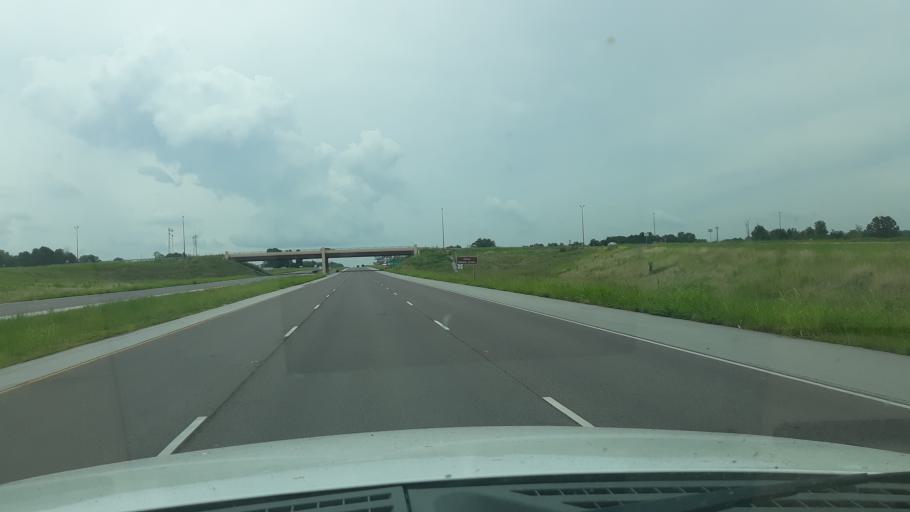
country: US
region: Illinois
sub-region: Williamson County
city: Crainville
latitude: 37.7450
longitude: -89.0617
